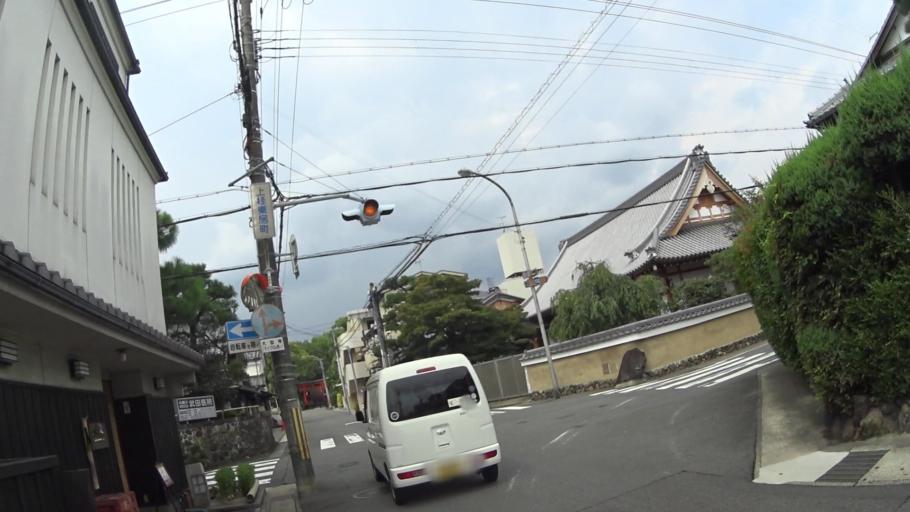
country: JP
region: Kyoto
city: Muko
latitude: 34.9907
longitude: 135.6996
